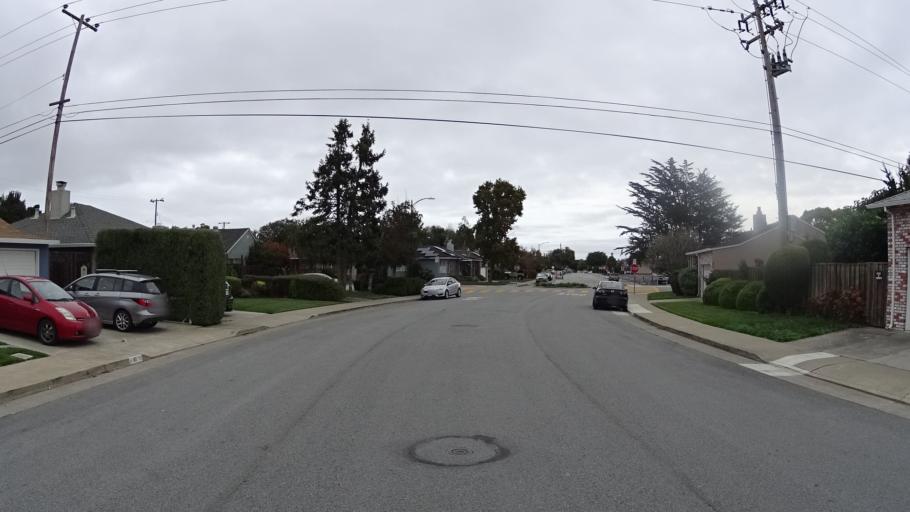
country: US
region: California
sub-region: San Mateo County
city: Belmont
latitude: 37.5373
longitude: -122.2925
